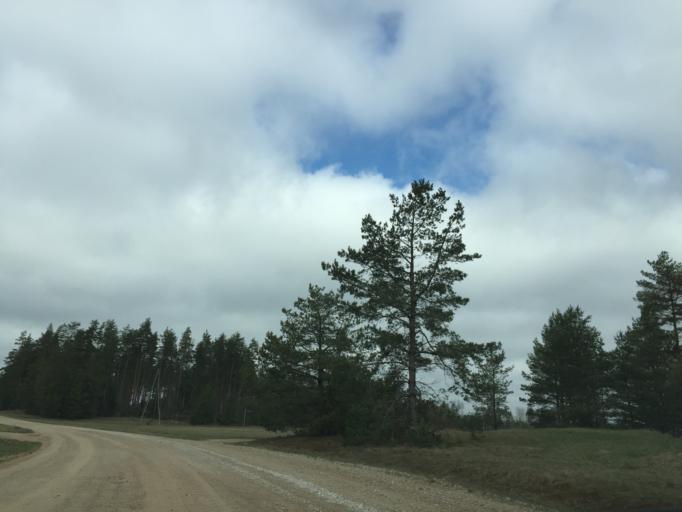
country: EE
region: Valgamaa
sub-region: Valga linn
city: Valga
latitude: 57.6445
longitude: 26.2271
